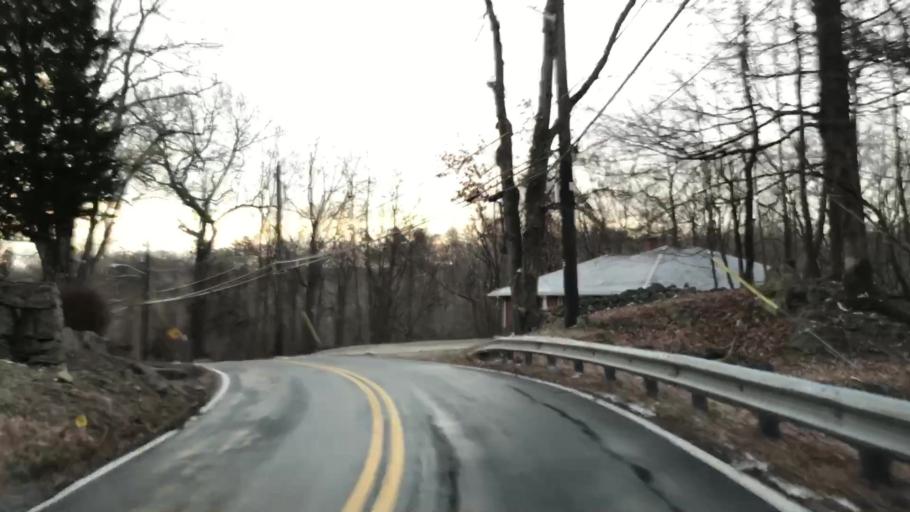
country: US
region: New York
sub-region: Rockland County
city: Stony Point
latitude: 41.2339
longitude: -74.0025
